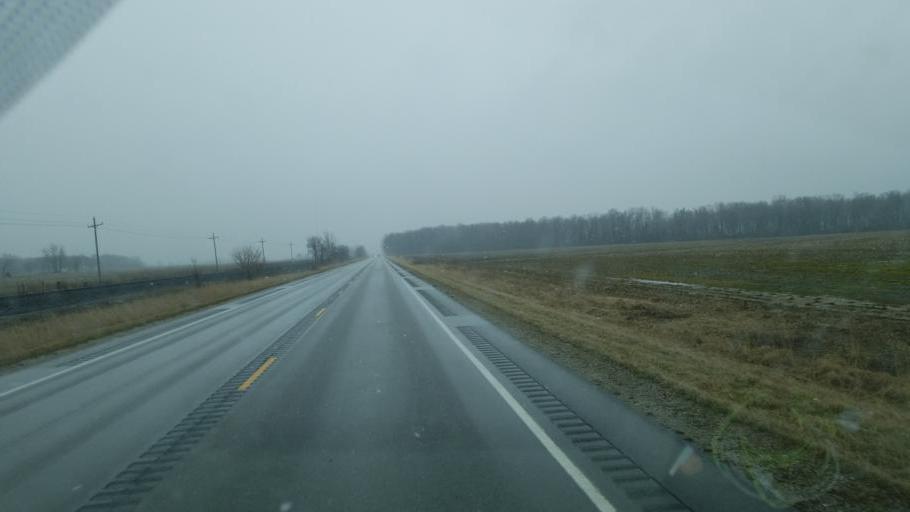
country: US
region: Indiana
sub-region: Wabash County
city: Mount Vernon
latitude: 40.7081
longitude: -85.7631
